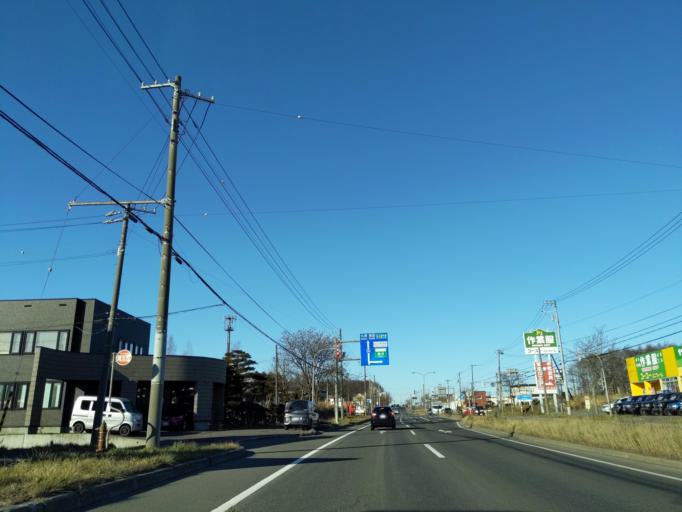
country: JP
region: Hokkaido
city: Kitahiroshima
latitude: 42.9423
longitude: 141.5033
